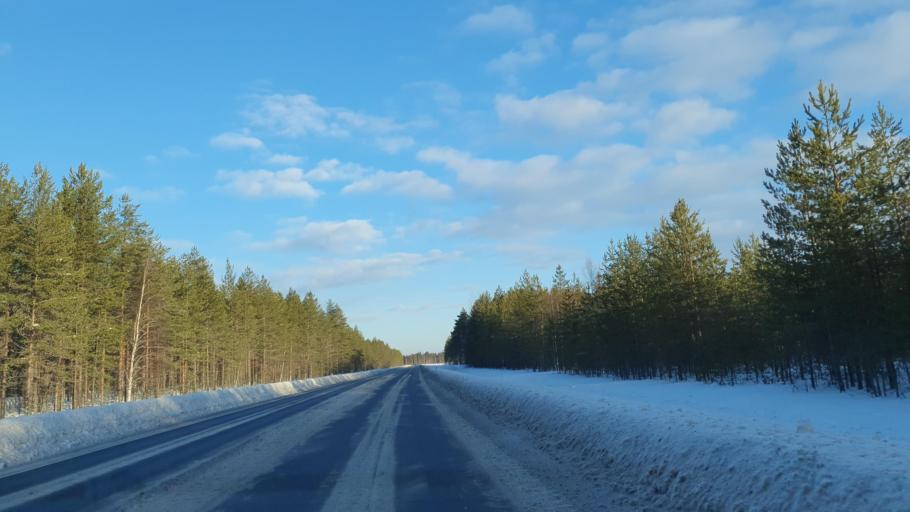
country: FI
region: Northern Ostrobothnia
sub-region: Oulunkaari
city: Utajaervi
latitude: 64.7085
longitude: 26.5167
